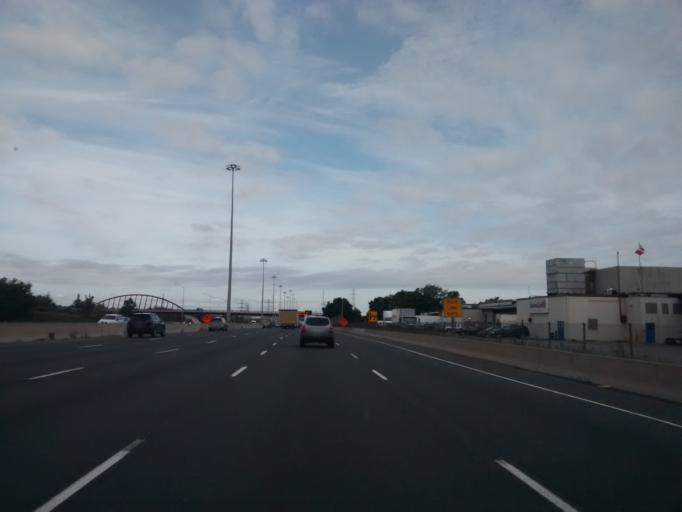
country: CA
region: Ontario
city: Hamilton
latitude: 43.2491
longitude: -79.7613
